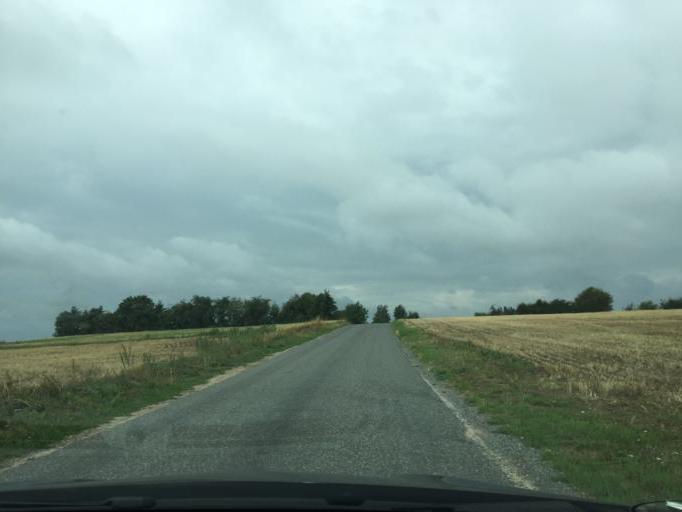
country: DK
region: South Denmark
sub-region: Assens Kommune
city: Harby
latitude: 55.1882
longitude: 10.0663
